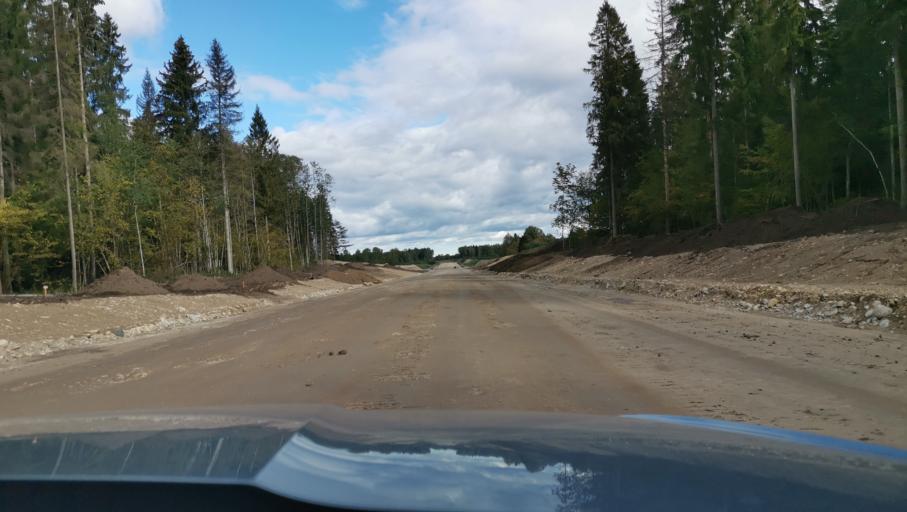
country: EE
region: Harju
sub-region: Nissi vald
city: Riisipere
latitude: 59.1396
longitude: 24.4886
